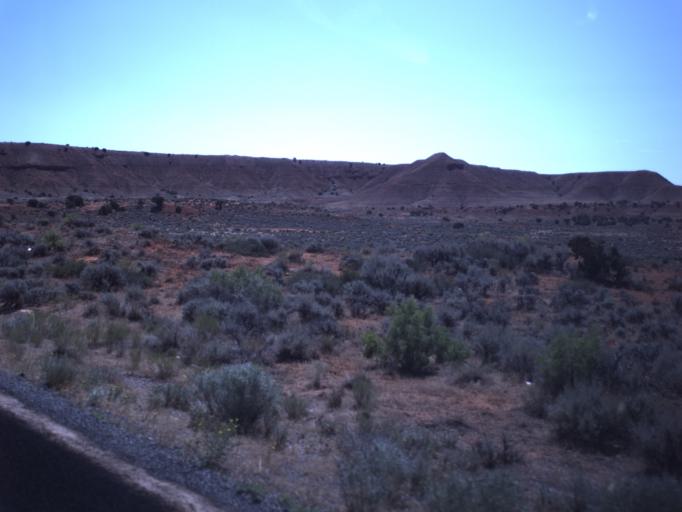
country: US
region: Utah
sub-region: Uintah County
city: Maeser
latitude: 40.4112
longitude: -109.7251
